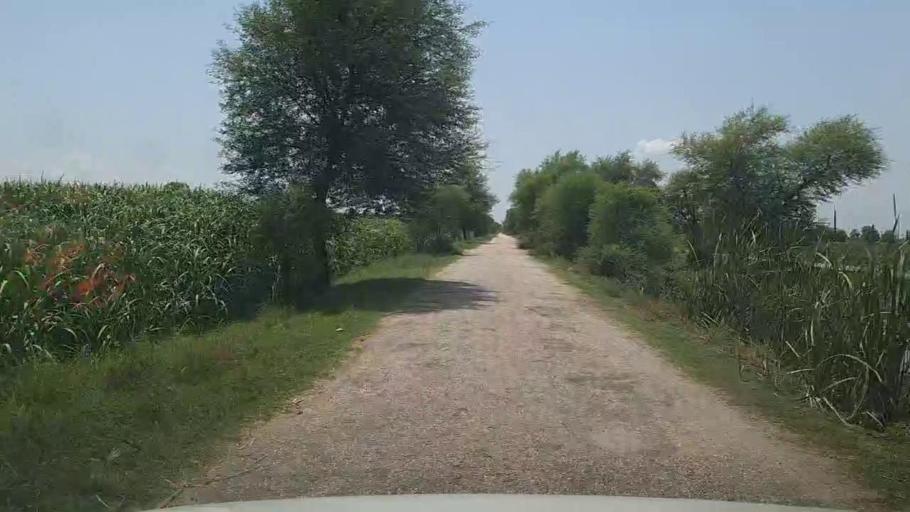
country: PK
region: Sindh
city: Ubauro
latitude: 28.1604
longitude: 69.7453
